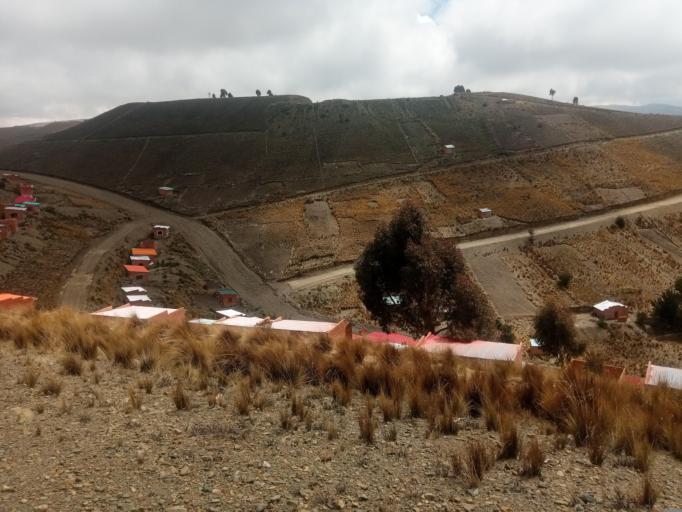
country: BO
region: La Paz
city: La Paz
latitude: -16.4634
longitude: -68.1376
